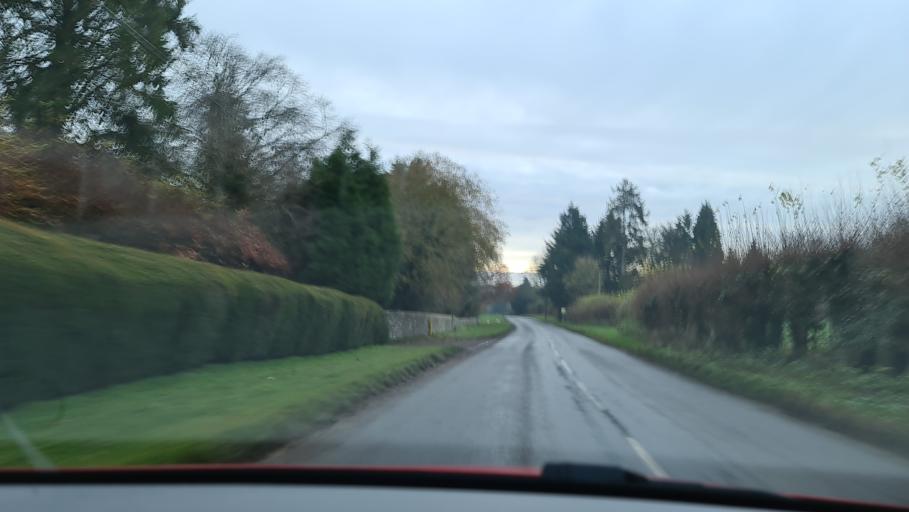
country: GB
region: England
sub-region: Buckinghamshire
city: Great Missenden
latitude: 51.7104
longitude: -0.7278
